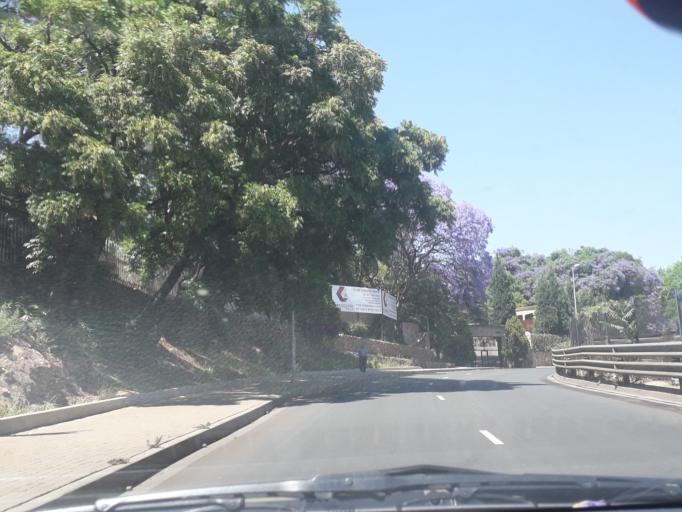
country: ZA
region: Gauteng
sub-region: City of Johannesburg Metropolitan Municipality
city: Johannesburg
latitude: -26.1707
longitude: 28.0736
